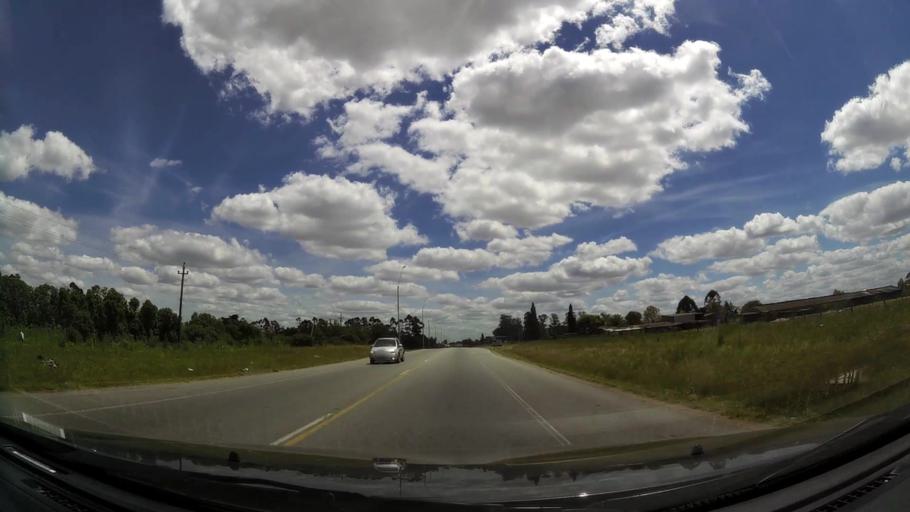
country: UY
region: Canelones
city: Colonia Nicolich
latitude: -34.8056
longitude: -56.0053
